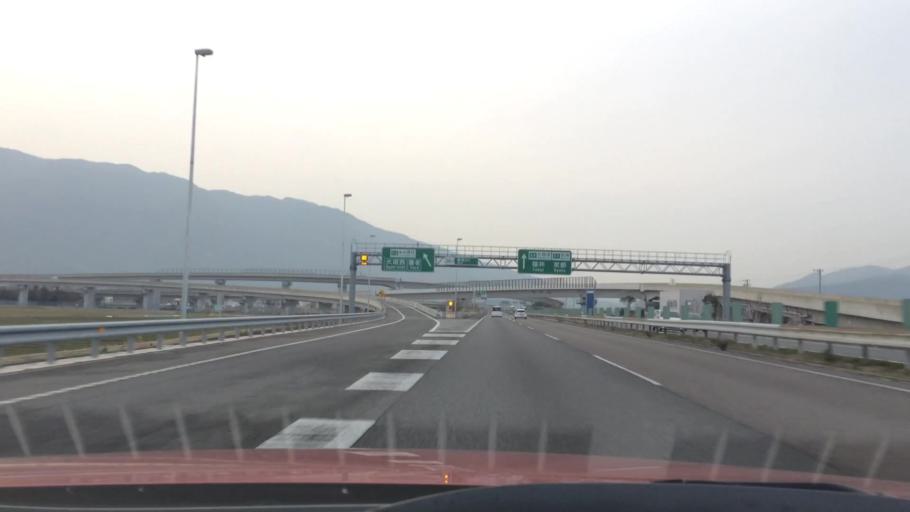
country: JP
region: Gifu
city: Ogaki
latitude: 35.3182
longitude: 136.5741
